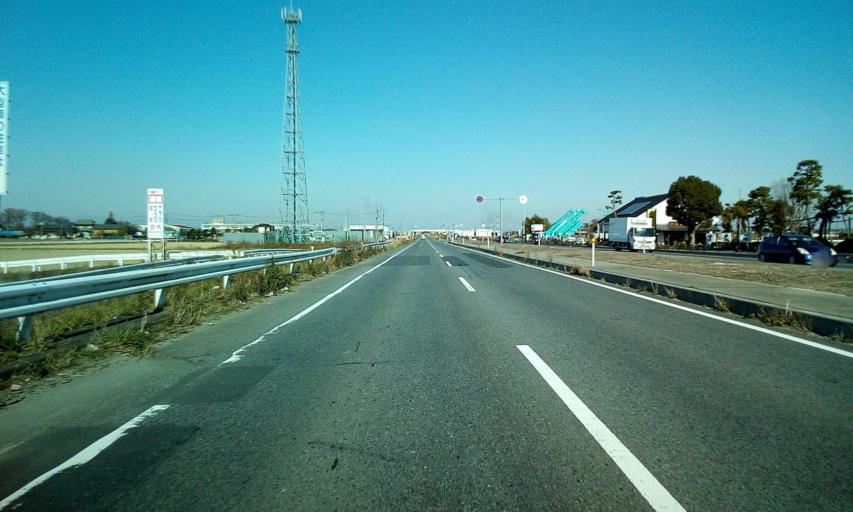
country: JP
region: Saitama
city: Satte
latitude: 36.0599
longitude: 139.7725
